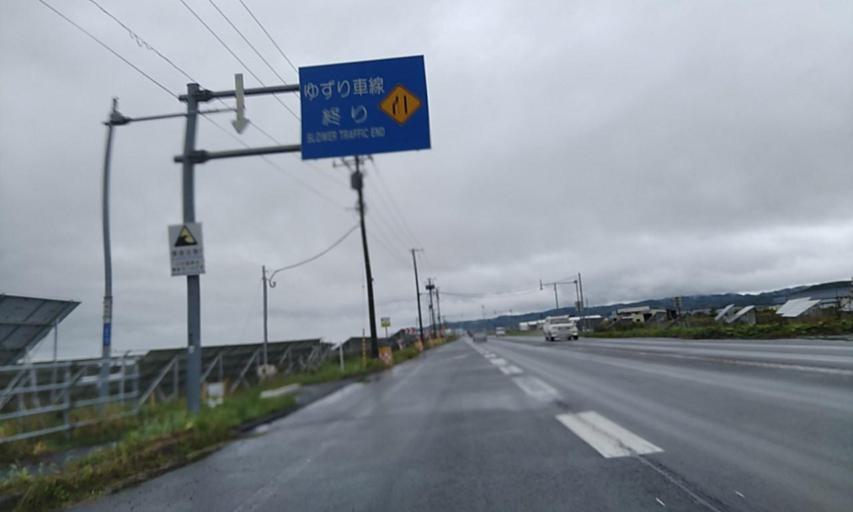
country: JP
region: Hokkaido
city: Kushiro
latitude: 42.9860
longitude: 144.1722
